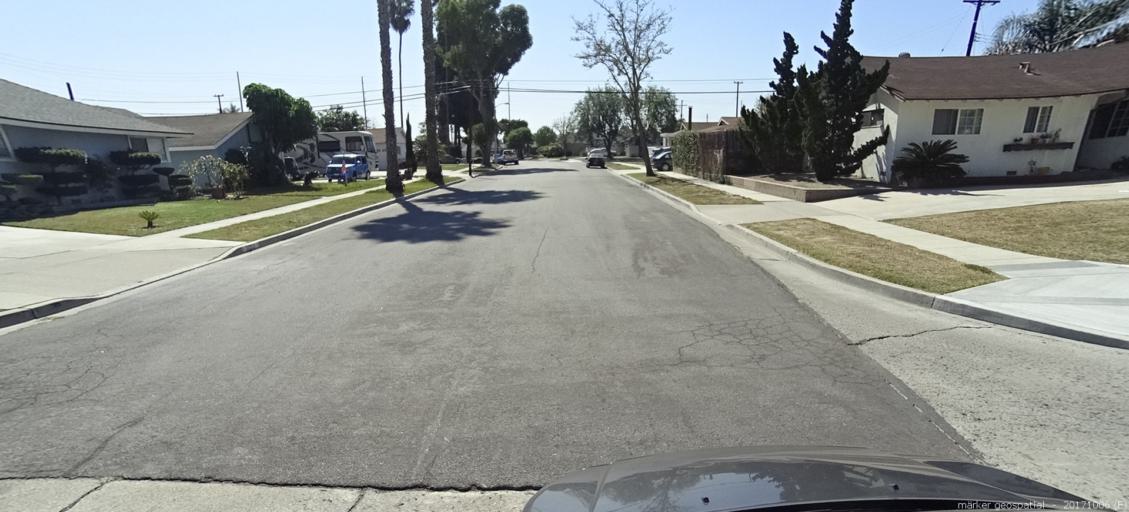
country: US
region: California
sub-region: Orange County
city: Stanton
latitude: 33.7846
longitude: -117.9954
